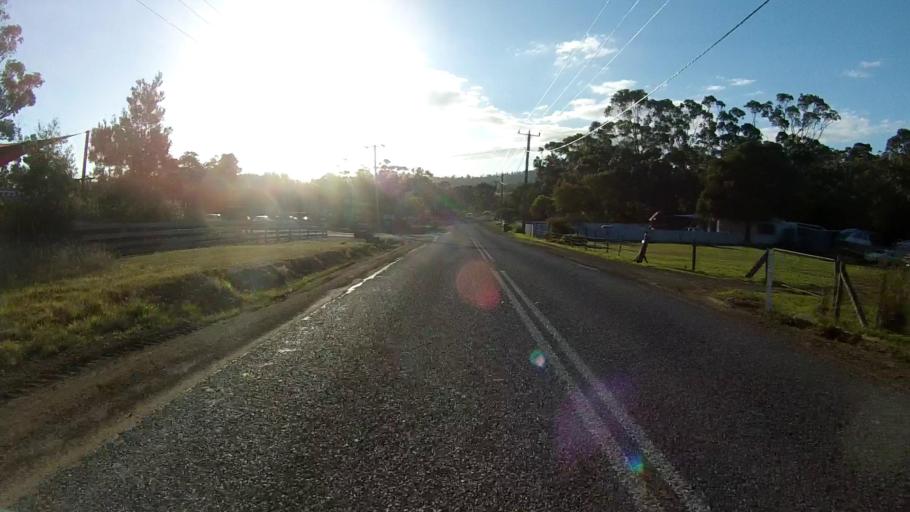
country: AU
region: Tasmania
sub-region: Sorell
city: Sorell
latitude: -42.9487
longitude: 147.8673
